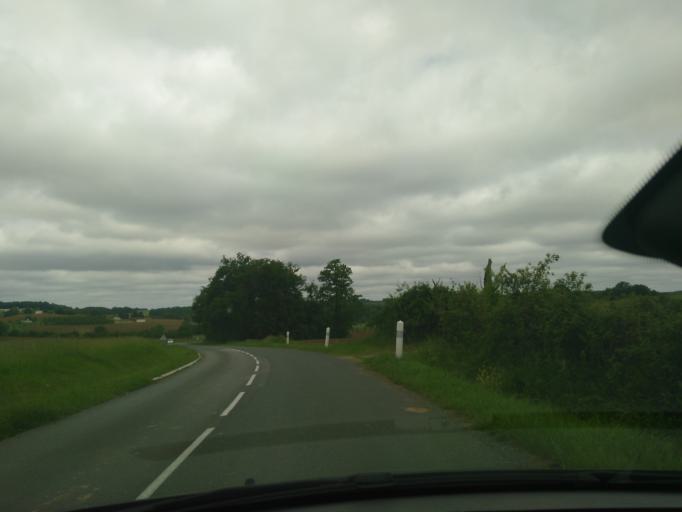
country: FR
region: Aquitaine
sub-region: Departement du Lot-et-Garonne
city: Cancon
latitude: 44.5453
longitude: 0.5798
